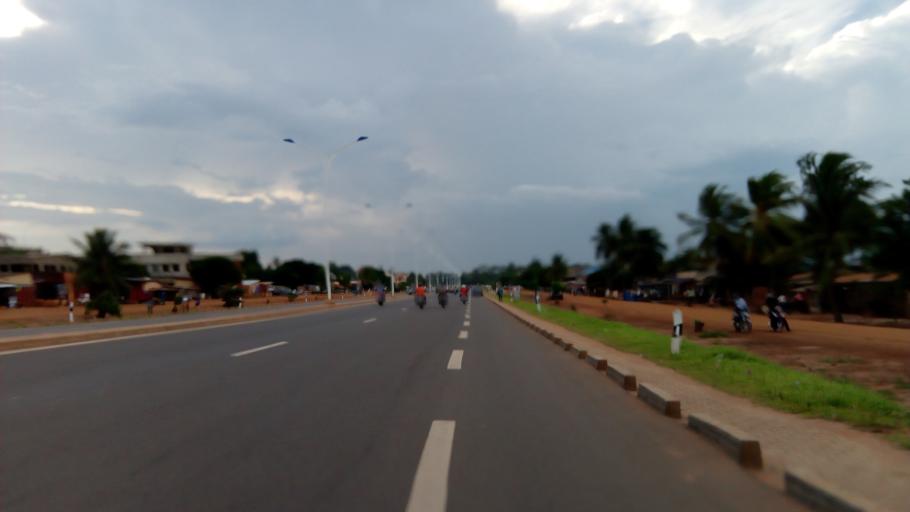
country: TG
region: Maritime
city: Lome
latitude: 6.2430
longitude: 1.1970
